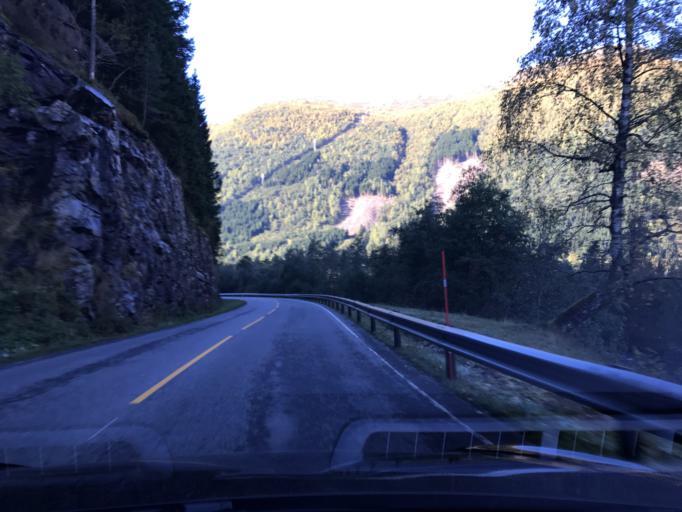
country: NO
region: More og Romsdal
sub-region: Norddal
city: Valldal
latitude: 62.3107
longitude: 7.2696
